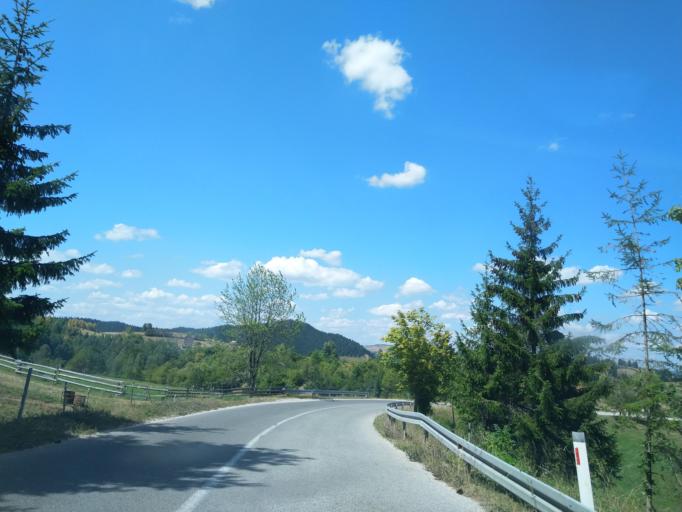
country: RS
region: Central Serbia
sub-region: Zlatiborski Okrug
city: Nova Varos
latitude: 43.4186
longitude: 19.8286
